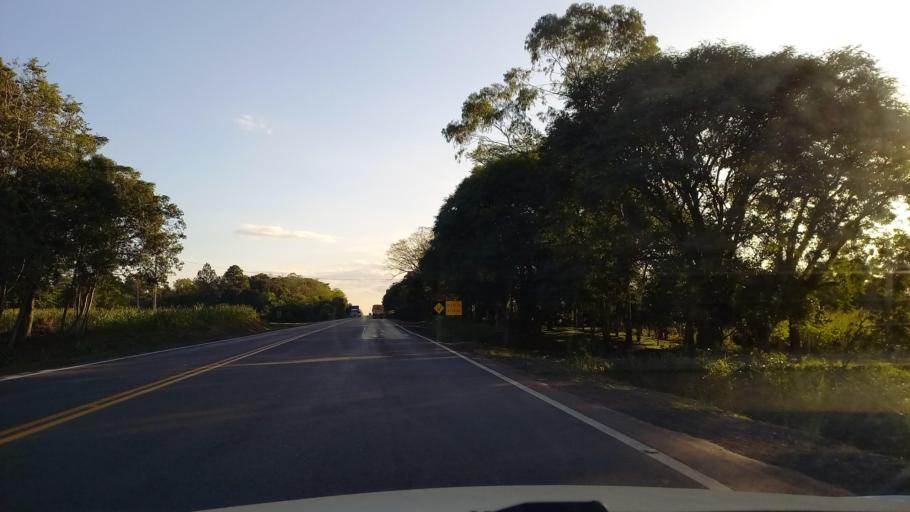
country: BR
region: Rio Grande do Sul
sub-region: Venancio Aires
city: Venancio Aires
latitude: -29.6581
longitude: -52.2365
